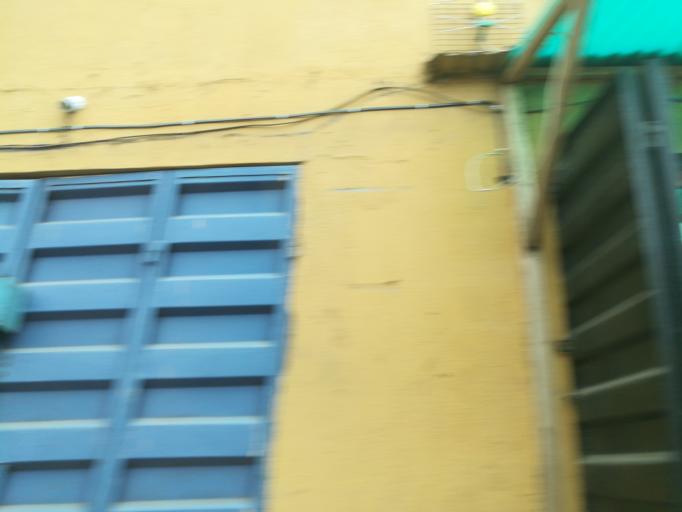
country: NG
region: Lagos
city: Ojota
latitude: 6.6005
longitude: 3.3846
